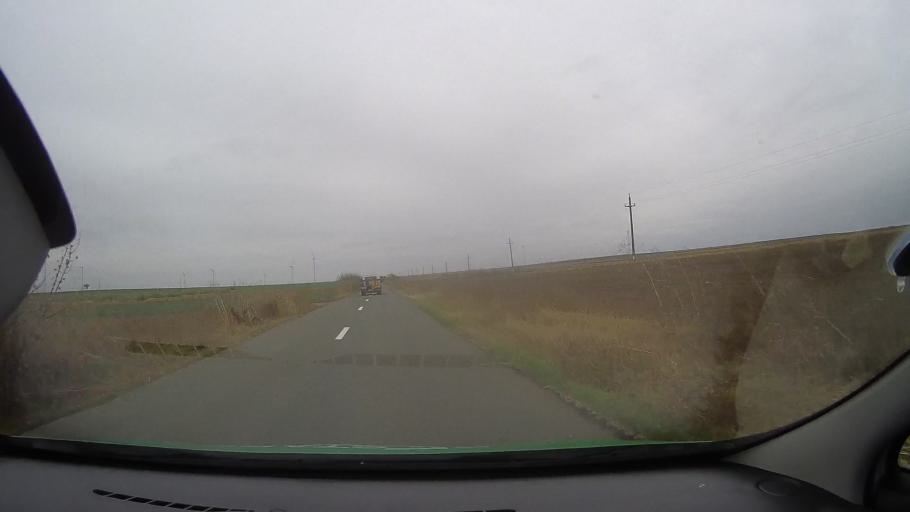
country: RO
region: Constanta
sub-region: Comuna Targusor
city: Targusor
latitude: 44.4681
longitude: 28.3915
